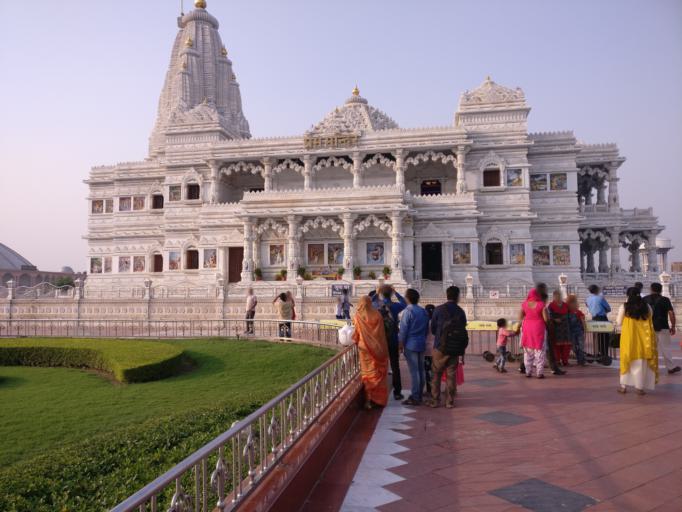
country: IN
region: Uttar Pradesh
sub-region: Mathura
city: Vrindavan
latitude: 27.5716
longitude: 77.6720
